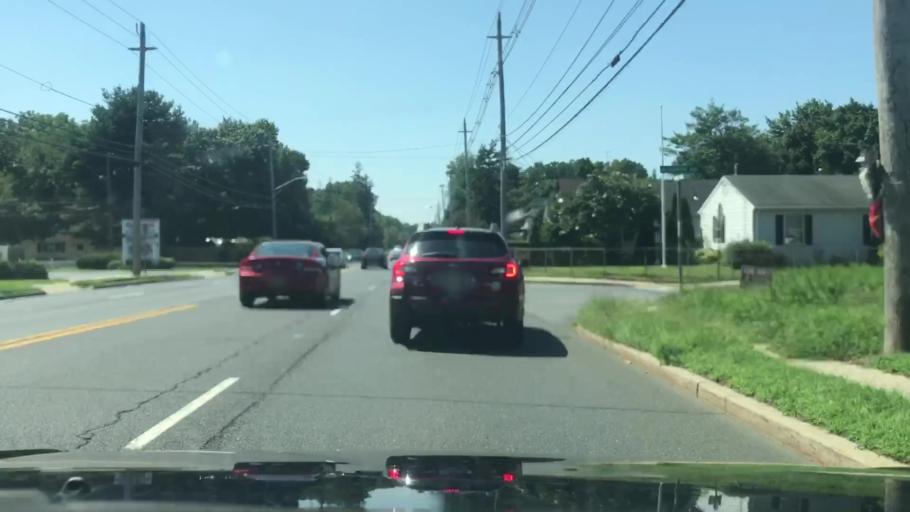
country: US
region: New Jersey
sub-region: Monmouth County
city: Red Bank
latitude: 40.3371
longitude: -74.0773
